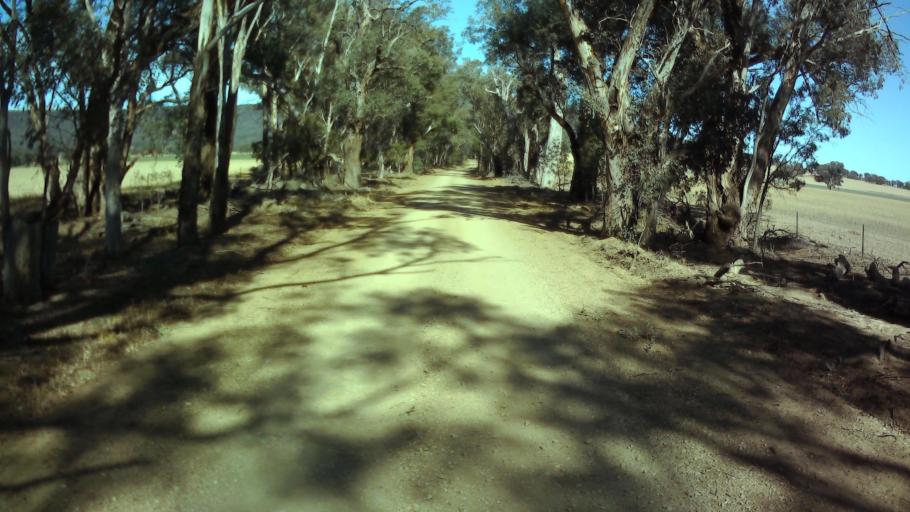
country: AU
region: New South Wales
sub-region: Weddin
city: Grenfell
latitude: -33.9020
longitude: 148.0343
